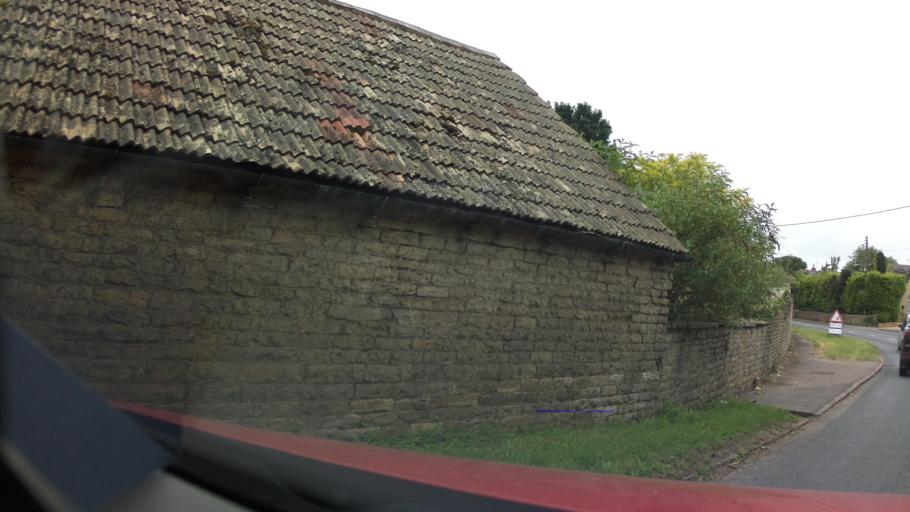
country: GB
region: England
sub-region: District of Rutland
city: Exton
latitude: 52.6688
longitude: -0.6331
